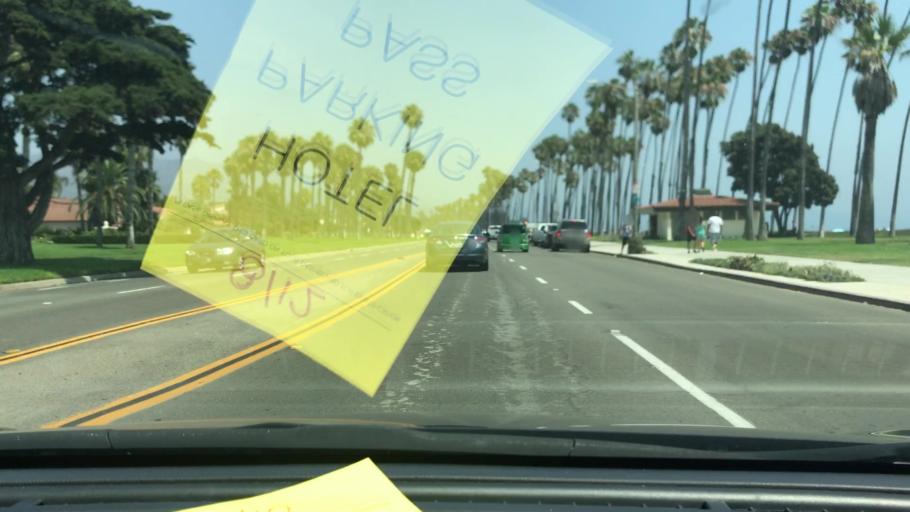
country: US
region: California
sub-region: Santa Barbara County
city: Santa Barbara
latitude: 34.4154
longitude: -119.6801
